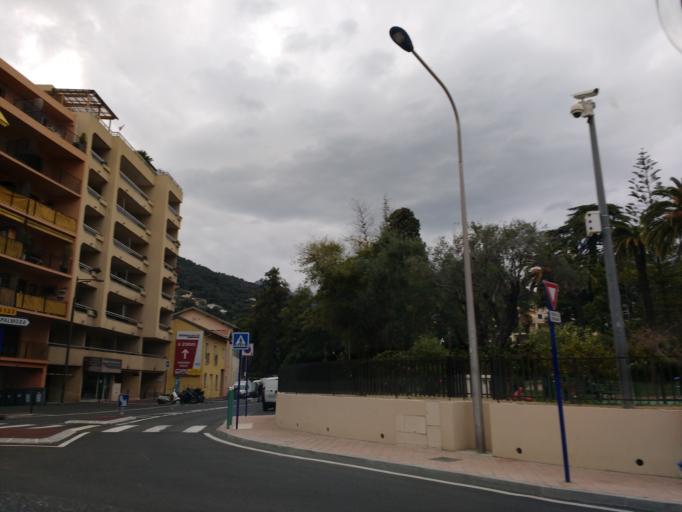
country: FR
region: Provence-Alpes-Cote d'Azur
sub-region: Departement des Alpes-Maritimes
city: Roquebrune-Cap-Martin
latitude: 43.7662
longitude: 7.4840
